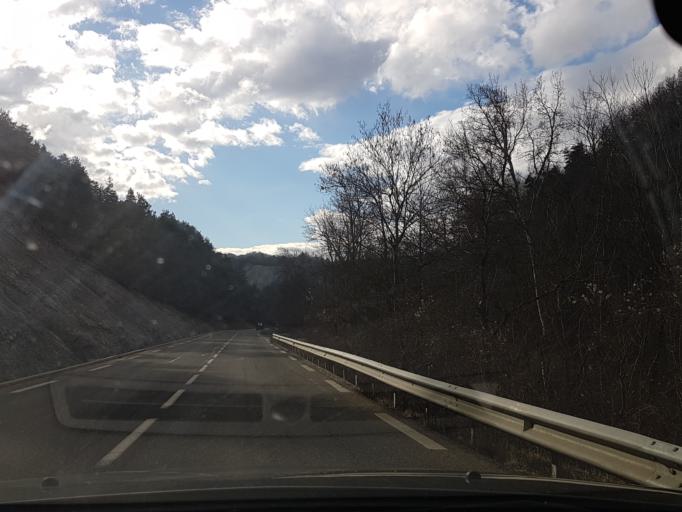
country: FR
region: Provence-Alpes-Cote d'Azur
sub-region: Departement des Hautes-Alpes
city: Gap
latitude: 44.5151
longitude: 6.0657
